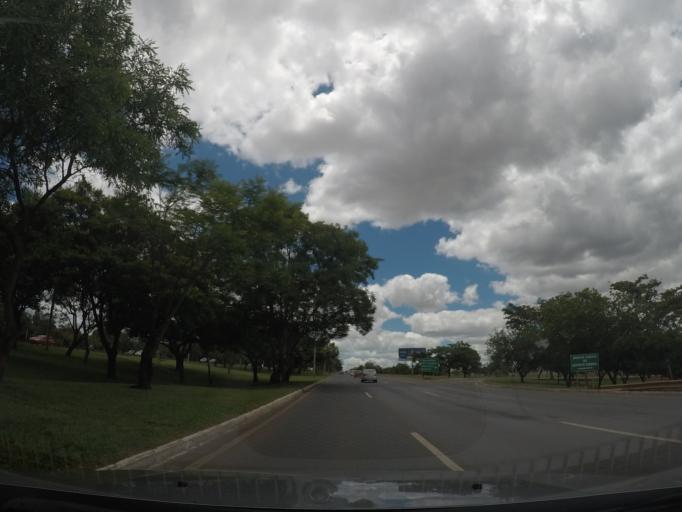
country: BR
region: Federal District
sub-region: Brasilia
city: Brasilia
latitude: -15.7577
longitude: -47.9281
